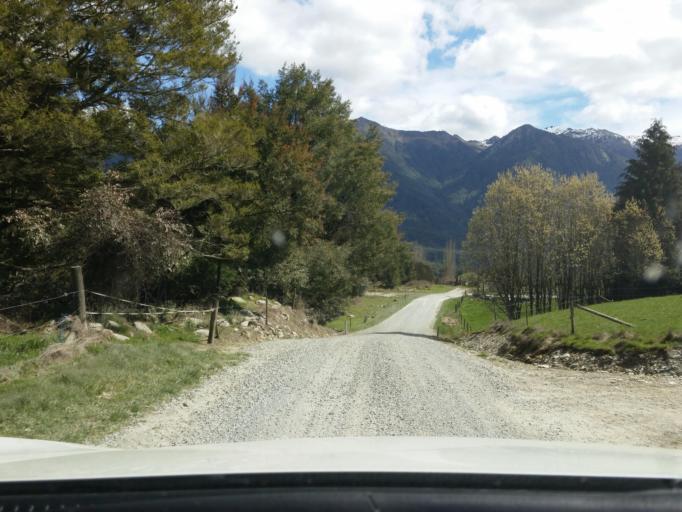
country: NZ
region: West Coast
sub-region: Buller District
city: Westport
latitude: -42.0081
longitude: 172.3564
